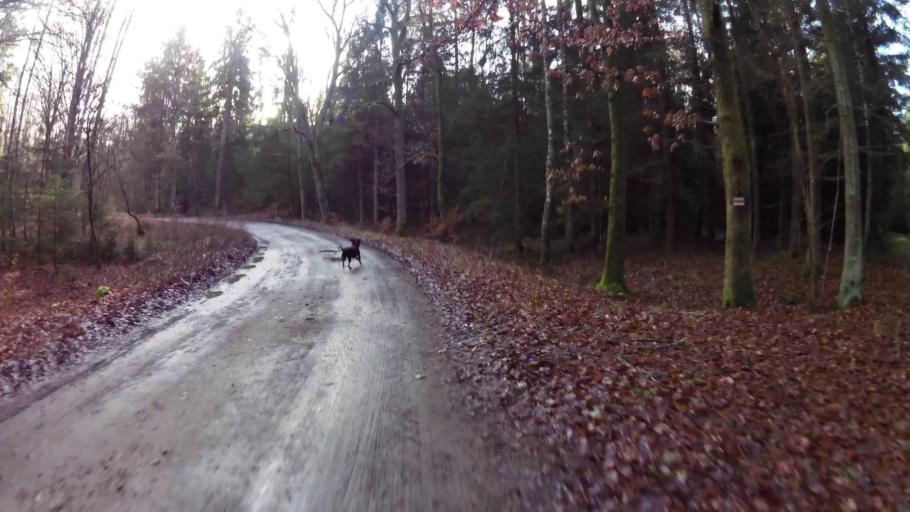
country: PL
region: West Pomeranian Voivodeship
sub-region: Powiat koszalinski
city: Sianow
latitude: 54.1154
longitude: 16.2959
